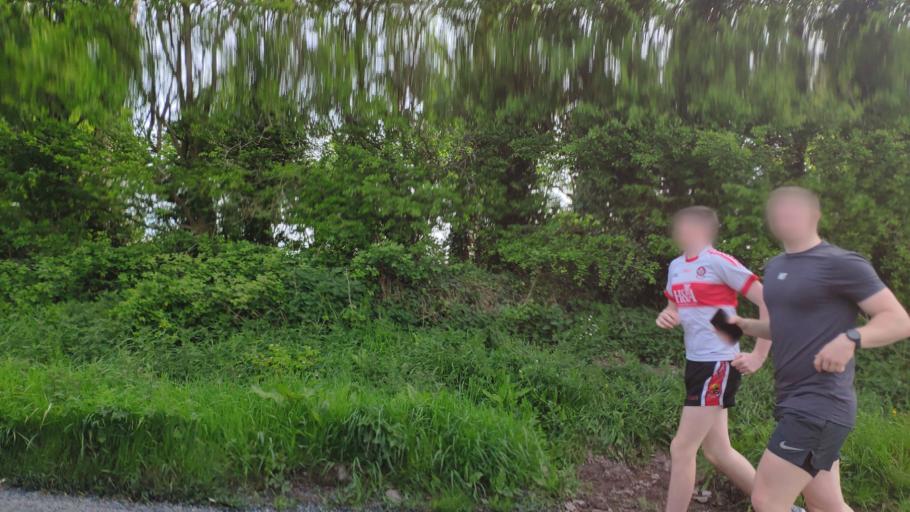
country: IE
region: Munster
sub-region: County Cork
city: Blarney
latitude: 51.9625
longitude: -8.5141
